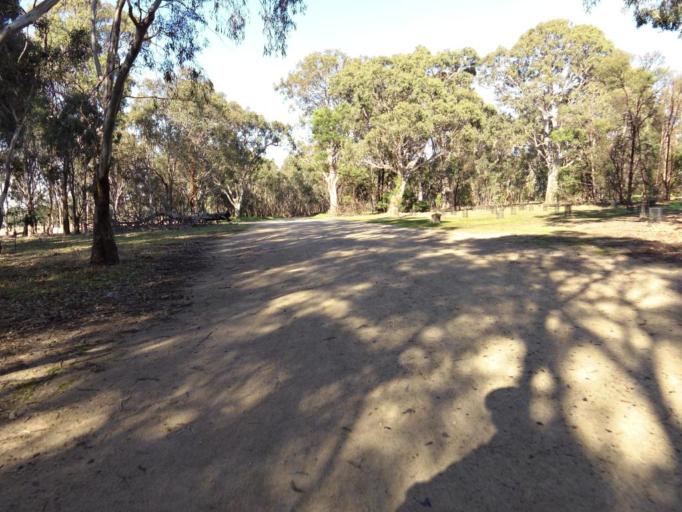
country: AU
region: Victoria
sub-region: Kingston
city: Waterways
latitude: -38.0048
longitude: 145.1329
